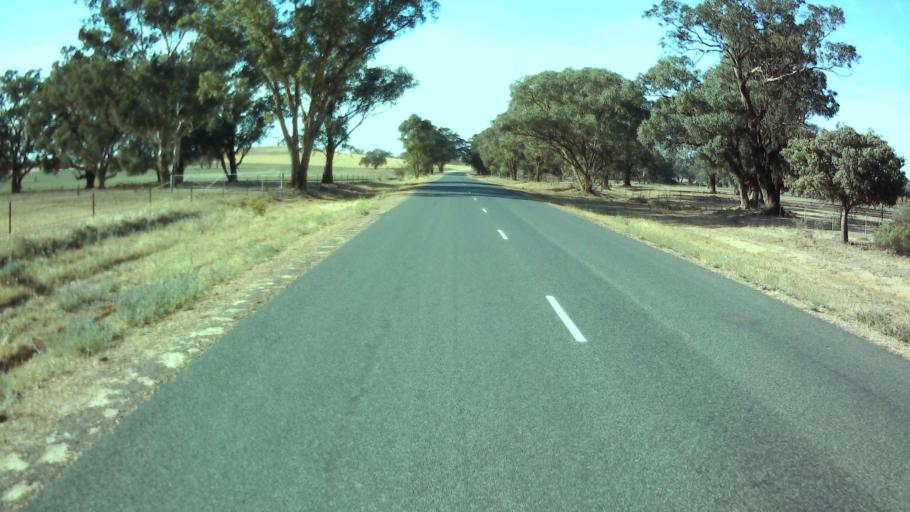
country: AU
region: New South Wales
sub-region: Weddin
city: Grenfell
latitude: -33.9637
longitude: 148.1404
